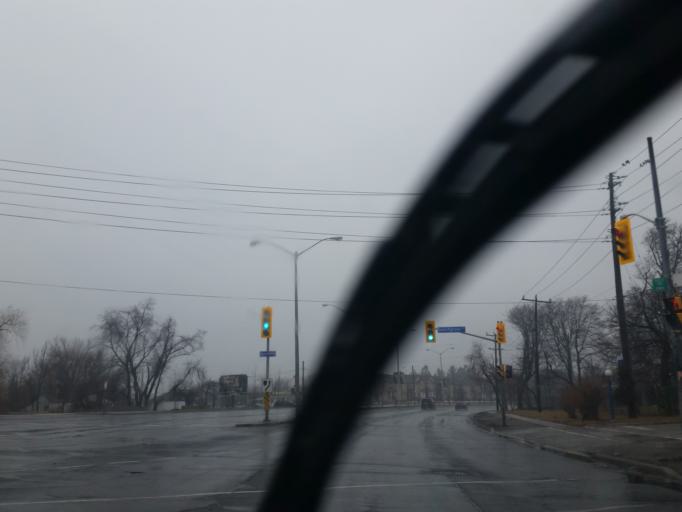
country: CA
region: Ontario
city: Scarborough
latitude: 43.7767
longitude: -79.1735
